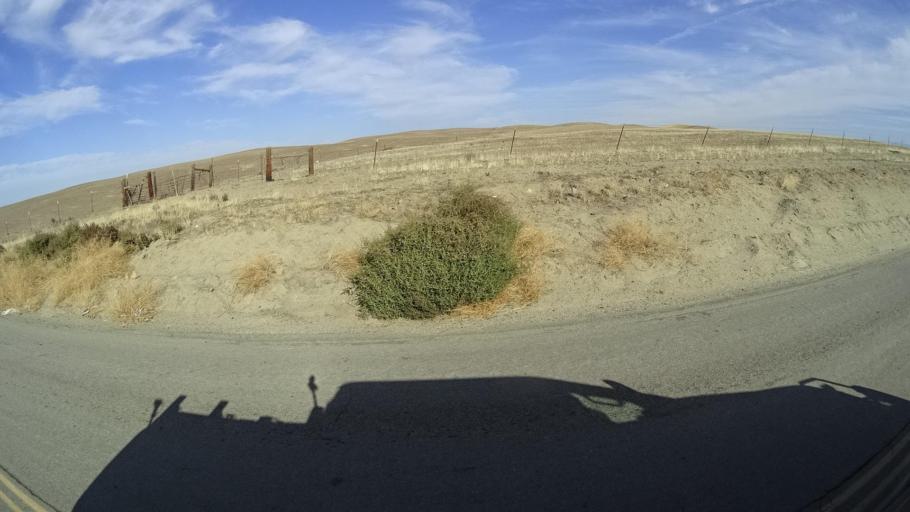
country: US
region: California
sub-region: Tulare County
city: Richgrove
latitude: 35.6223
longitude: -119.0098
